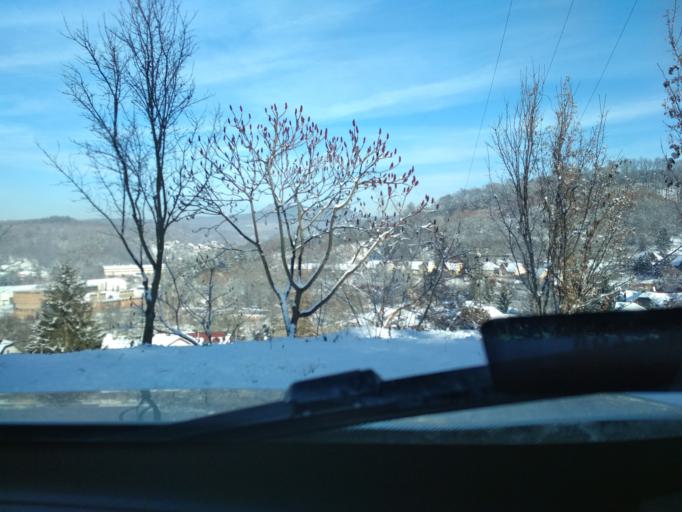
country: HU
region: Nograd
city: Salgotarjan
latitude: 48.1104
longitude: 19.8260
